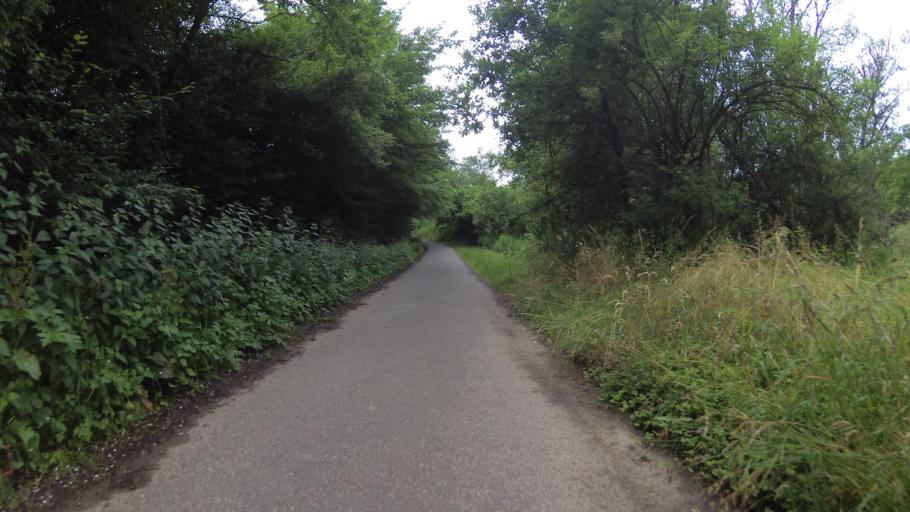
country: DE
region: Saarland
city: Marpingen
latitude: 49.4698
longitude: 7.0529
